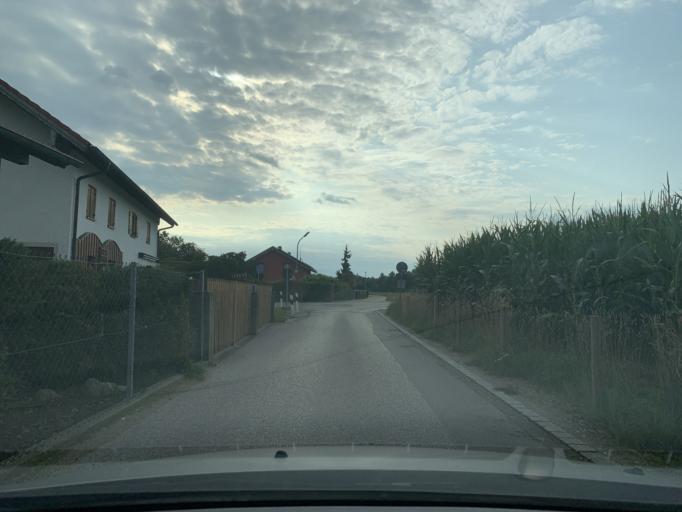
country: DE
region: Bavaria
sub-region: Upper Bavaria
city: Muehldorf
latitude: 48.2529
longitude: 12.5489
